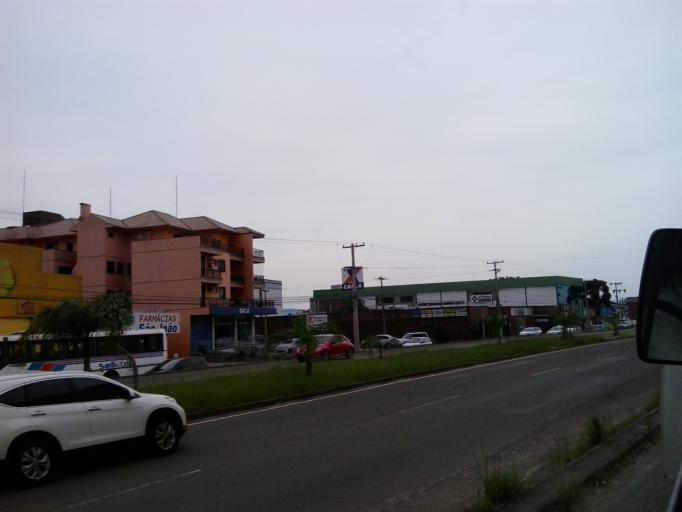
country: BR
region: Rio Grande do Sul
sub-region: Santa Maria
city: Santa Maria
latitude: -29.7017
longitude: -53.7190
